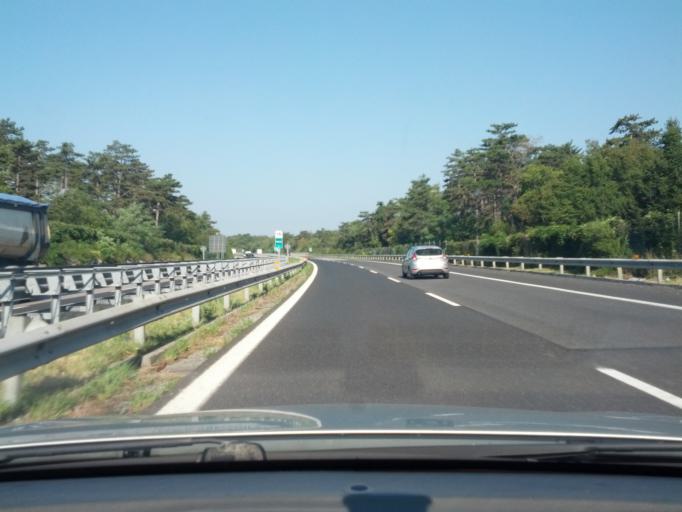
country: IT
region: Friuli Venezia Giulia
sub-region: Provincia di Trieste
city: Villa Opicina
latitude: 45.7024
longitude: 13.7962
